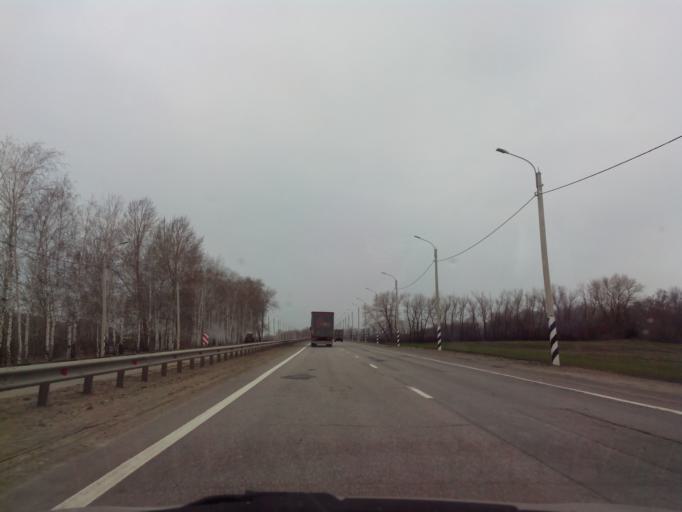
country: RU
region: Tambov
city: Selezni
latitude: 52.7488
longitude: 41.1875
